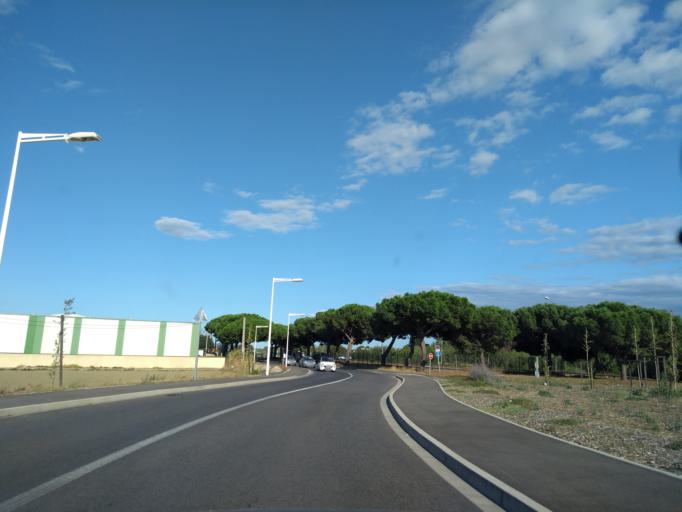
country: FR
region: Languedoc-Roussillon
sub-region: Departement des Pyrenees-Orientales
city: Perpignan
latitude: 42.7096
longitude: 2.9087
